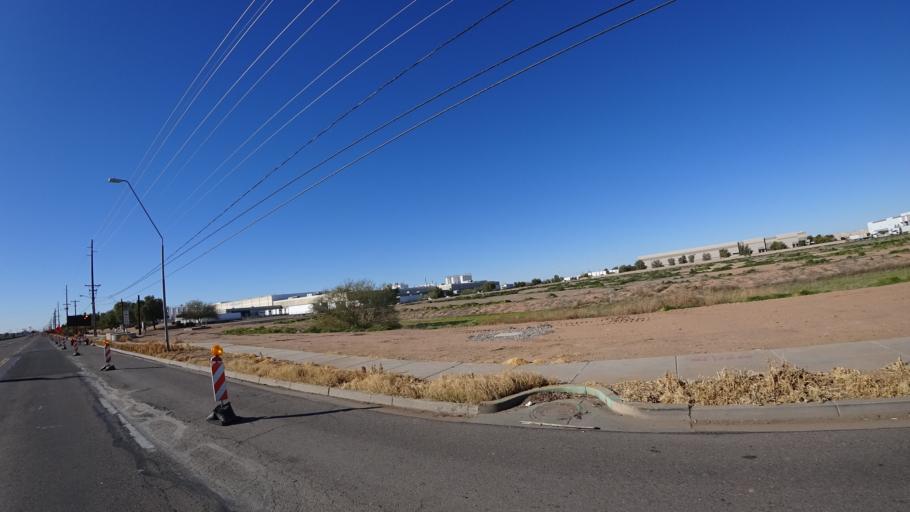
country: US
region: Arizona
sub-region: Maricopa County
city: Tolleson
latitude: 33.4358
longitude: -112.2628
